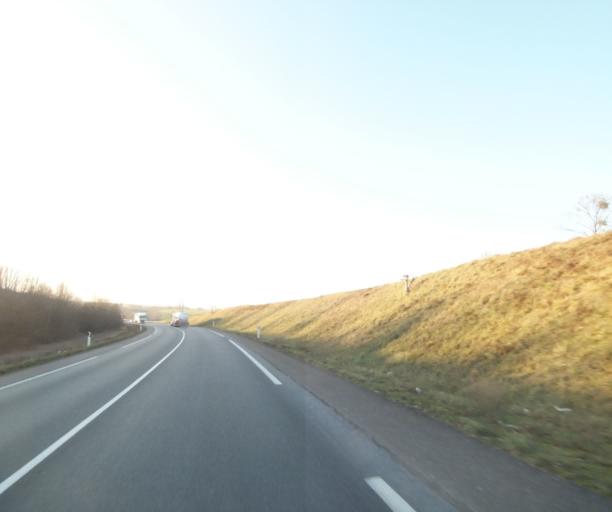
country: FR
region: Champagne-Ardenne
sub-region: Departement de la Haute-Marne
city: Bienville
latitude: 48.5455
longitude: 5.0767
